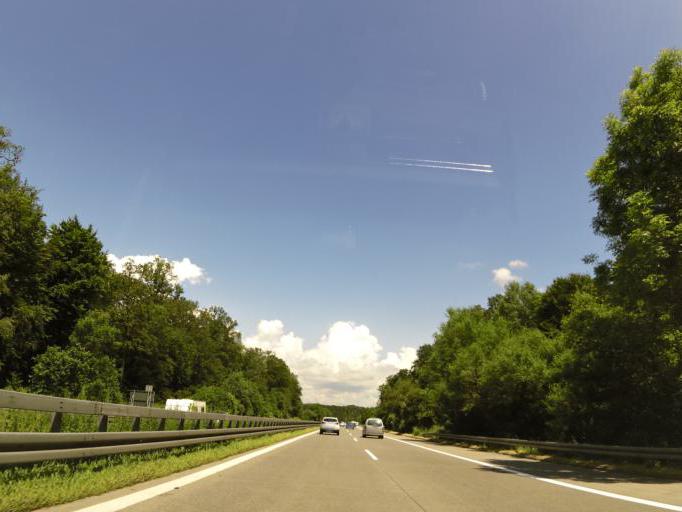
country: DE
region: Baden-Wuerttemberg
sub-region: Tuebingen Region
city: Nerenstetten
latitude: 48.5301
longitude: 10.0864
